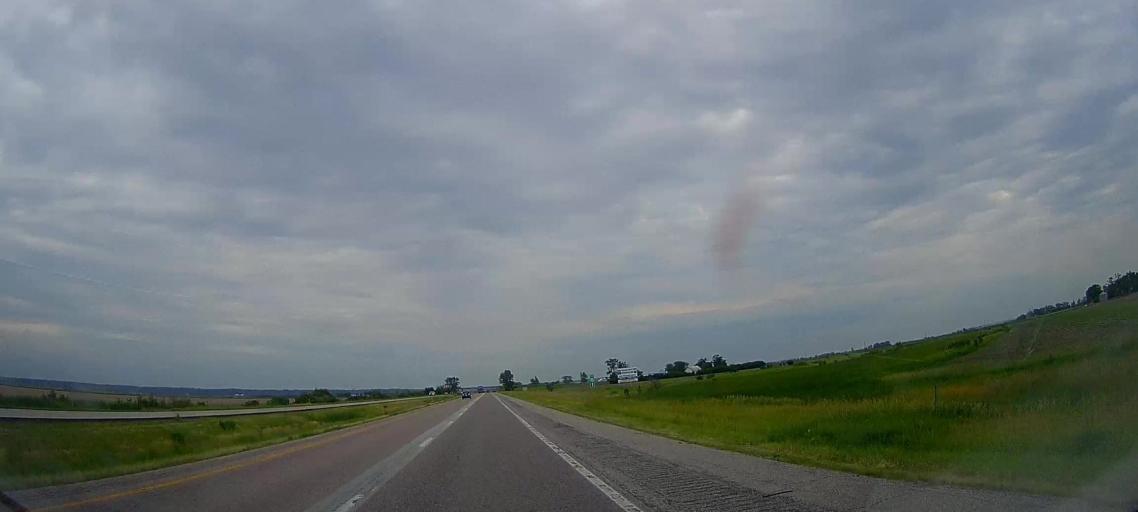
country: US
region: Iowa
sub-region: Harrison County
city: Missouri Valley
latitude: 41.6090
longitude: -95.9740
